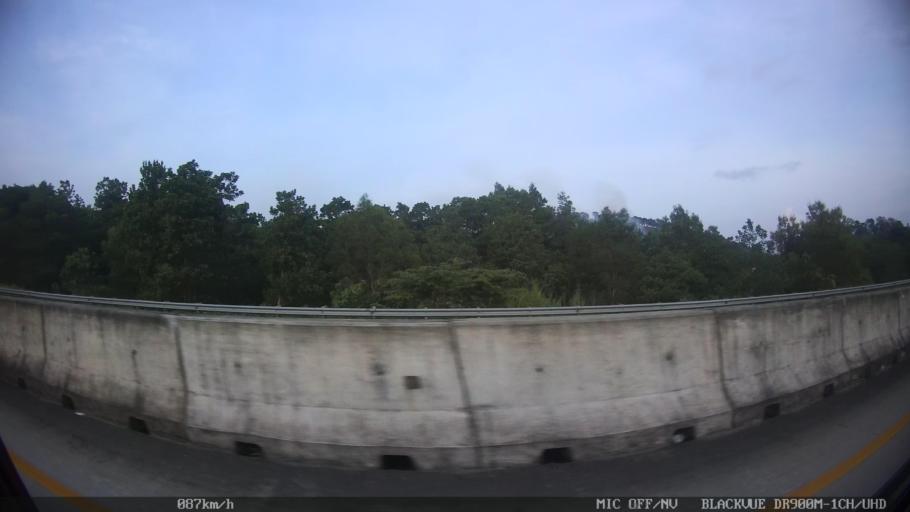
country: ID
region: Lampung
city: Penengahan
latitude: -5.8479
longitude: 105.7272
